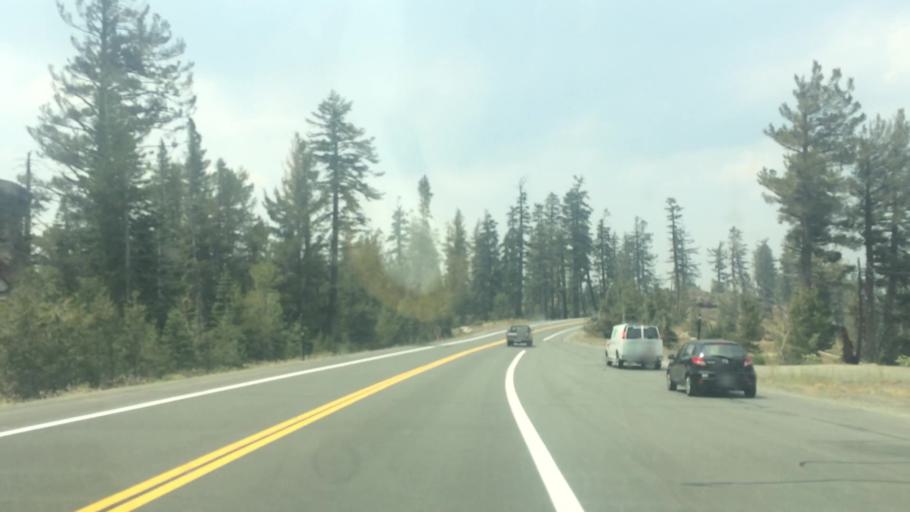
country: US
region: California
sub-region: El Dorado County
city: South Lake Tahoe
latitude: 38.6322
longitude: -120.1689
